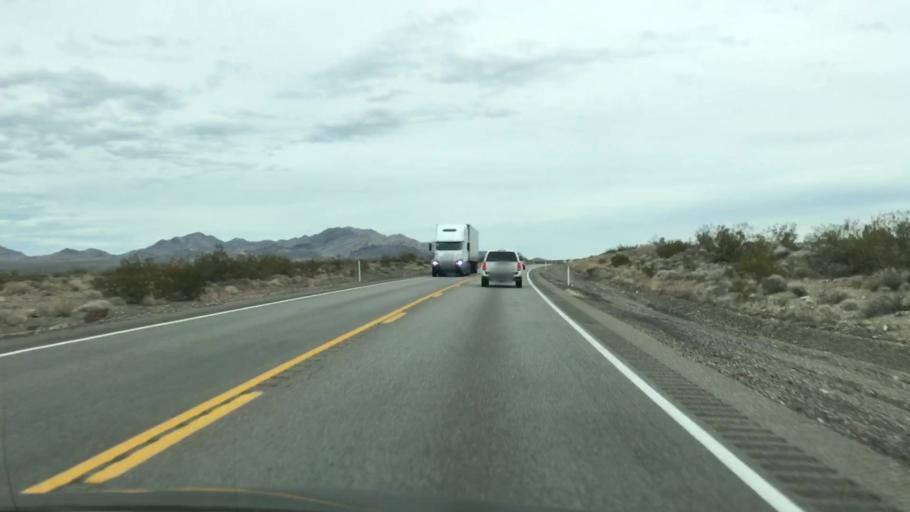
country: US
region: Nevada
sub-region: Nye County
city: Pahrump
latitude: 36.5878
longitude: -116.0532
